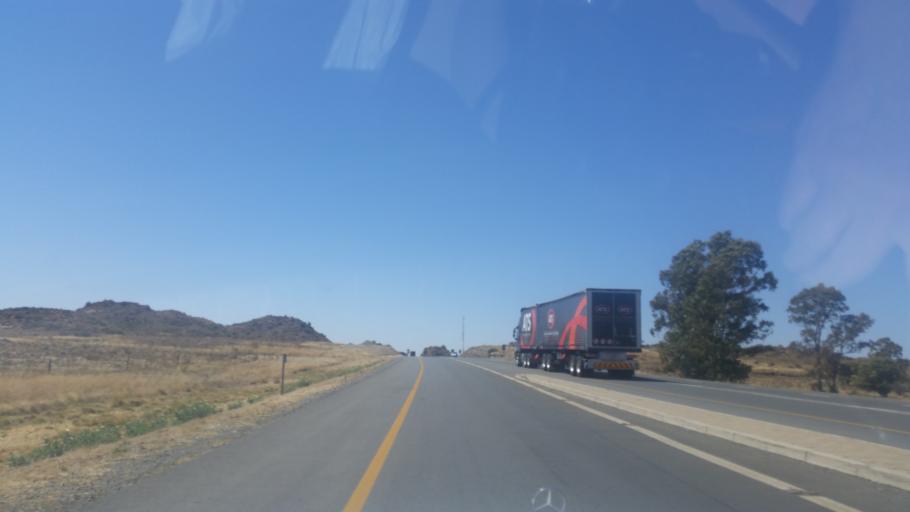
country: ZA
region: Northern Cape
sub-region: Pixley ka Seme District Municipality
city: Colesberg
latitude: -30.7237
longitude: 25.0883
